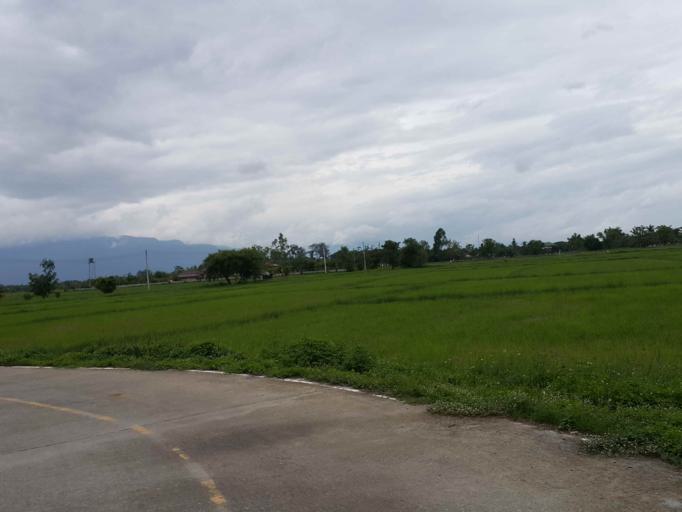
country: TH
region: Chiang Mai
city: San Sai
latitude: 18.8210
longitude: 99.0747
